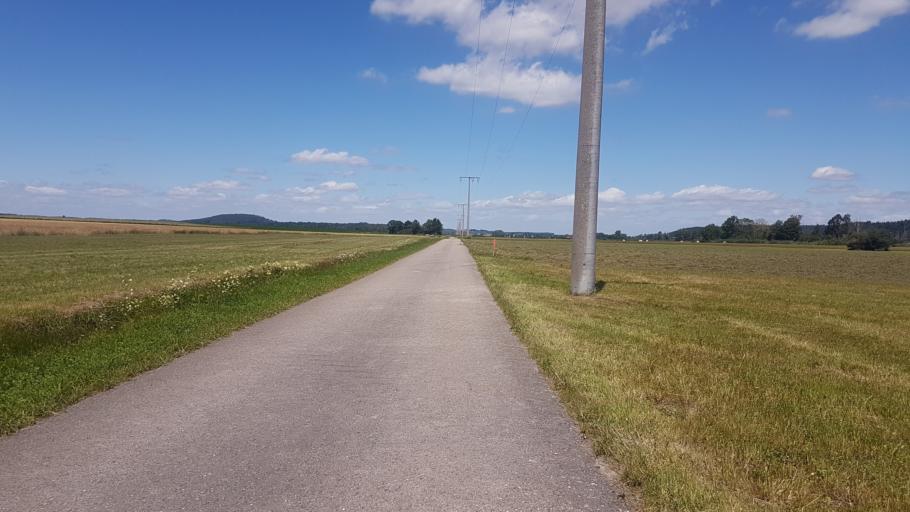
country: DE
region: Bavaria
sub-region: Regierungsbezirk Mittelfranken
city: Aurach
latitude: 49.2633
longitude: 10.4500
